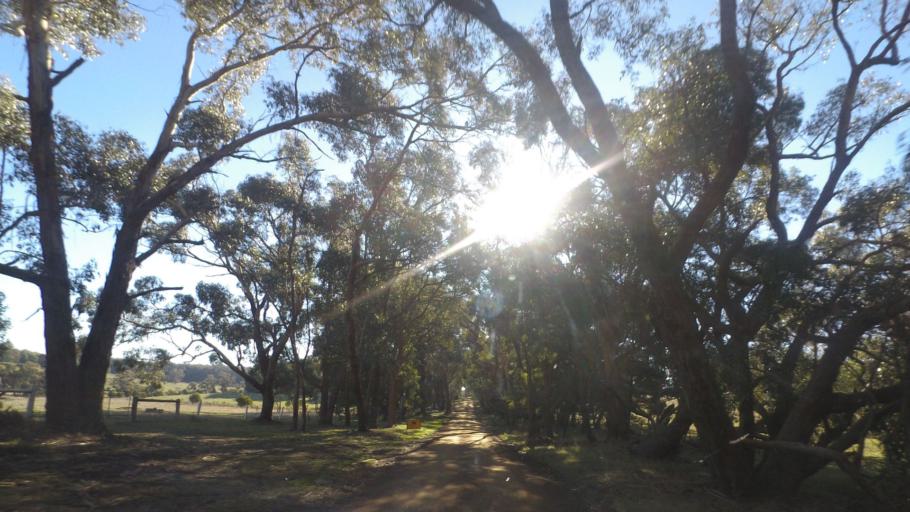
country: AU
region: Victoria
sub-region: Mount Alexander
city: Castlemaine
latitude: -37.2958
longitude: 144.3323
